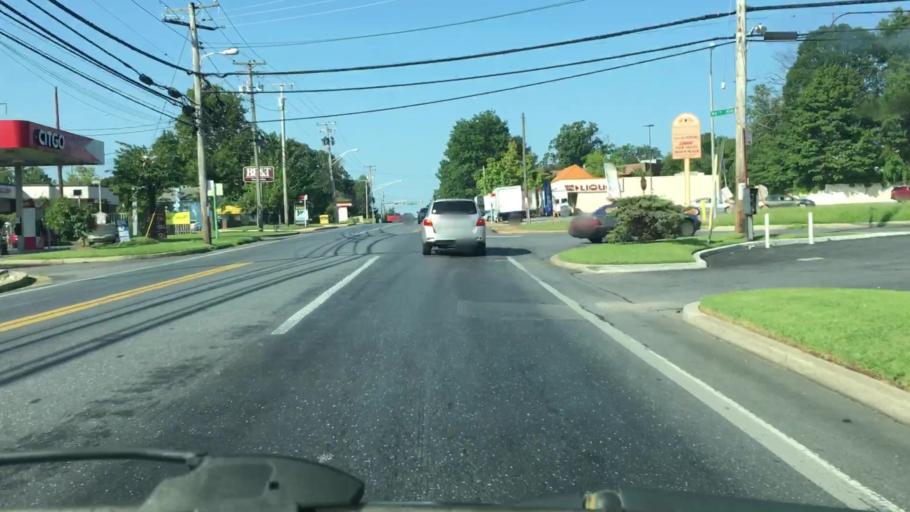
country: US
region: Maryland
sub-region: Prince George's County
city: Seabrook
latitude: 38.9723
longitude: -76.8470
